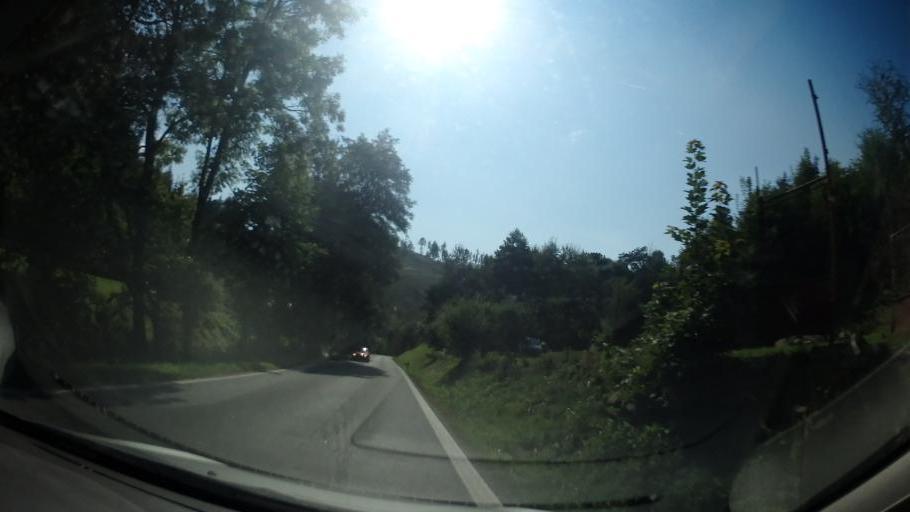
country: CZ
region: Pardubicky
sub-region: Okres Svitavy
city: Bystre
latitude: 49.5680
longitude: 16.3439
